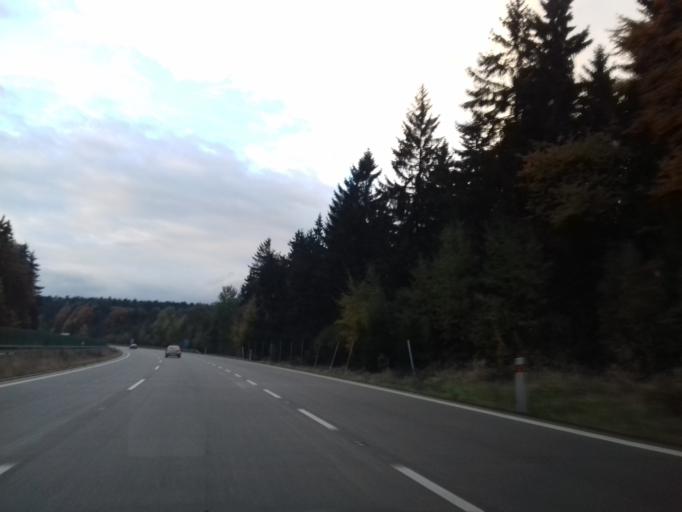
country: CZ
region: Vysocina
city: Stoky
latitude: 49.4765
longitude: 15.5628
